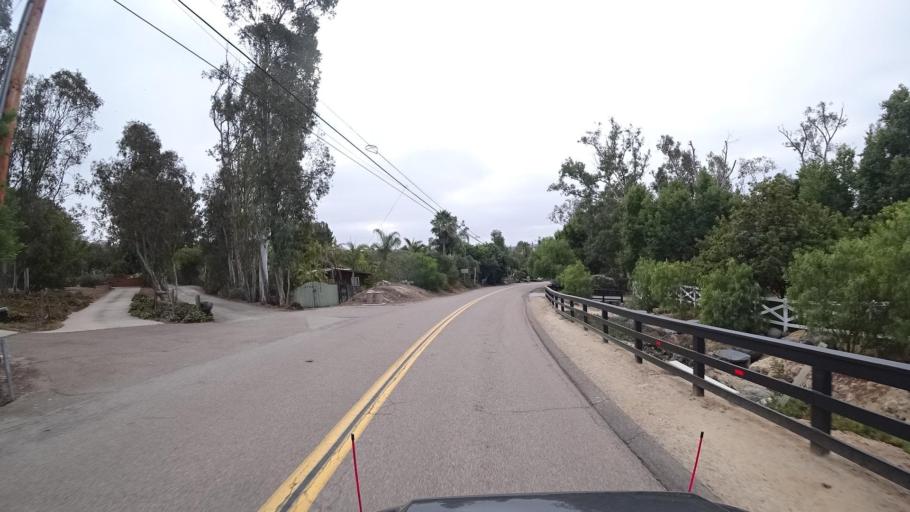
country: US
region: California
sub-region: San Diego County
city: Rancho Santa Fe
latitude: 32.9931
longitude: -117.2301
